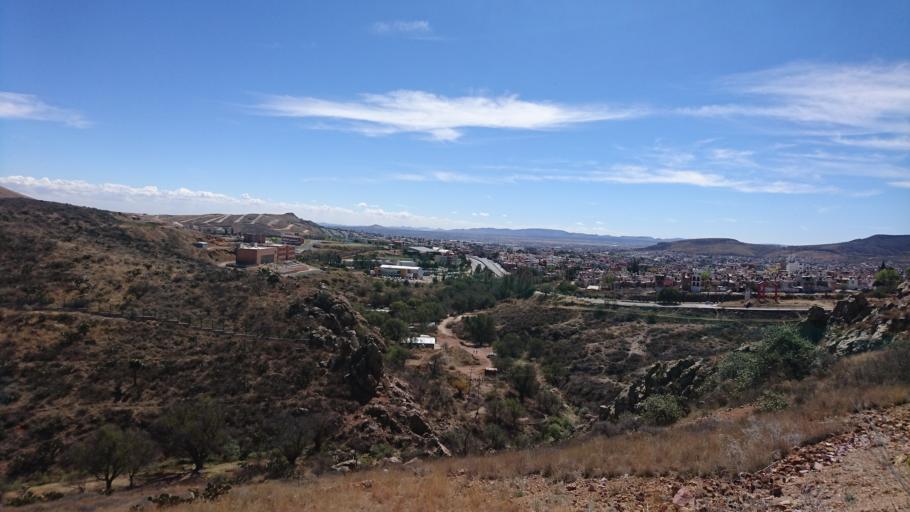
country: MX
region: Zacatecas
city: Zacatecas
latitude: 22.7761
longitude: -102.5465
